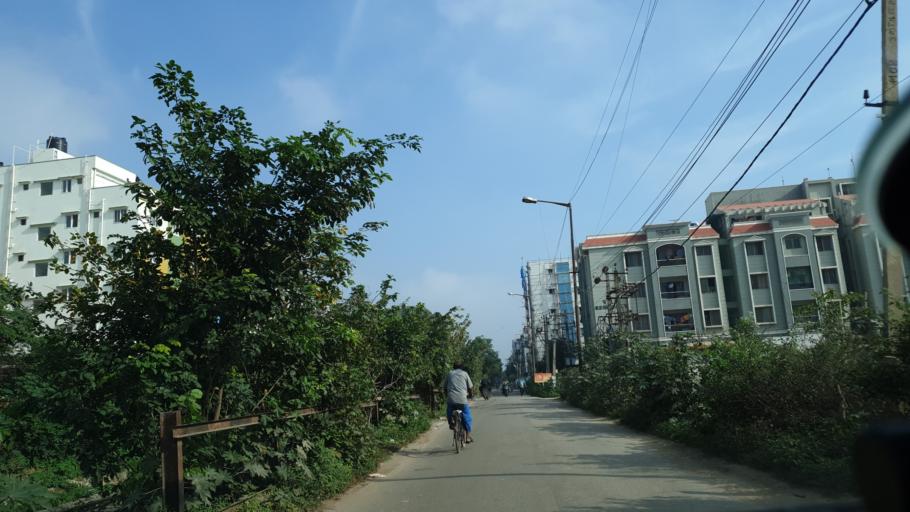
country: IN
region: Karnataka
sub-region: Bangalore Urban
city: Bangalore
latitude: 12.9599
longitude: 77.7043
